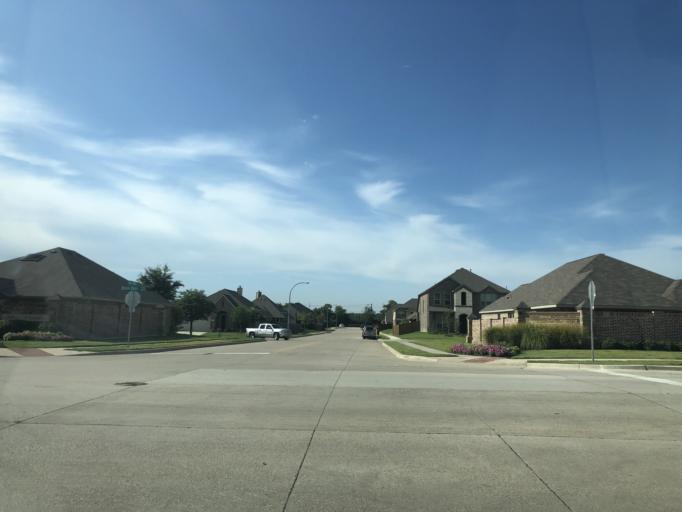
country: US
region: Texas
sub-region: Tarrant County
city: Haslet
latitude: 33.0184
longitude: -97.3058
